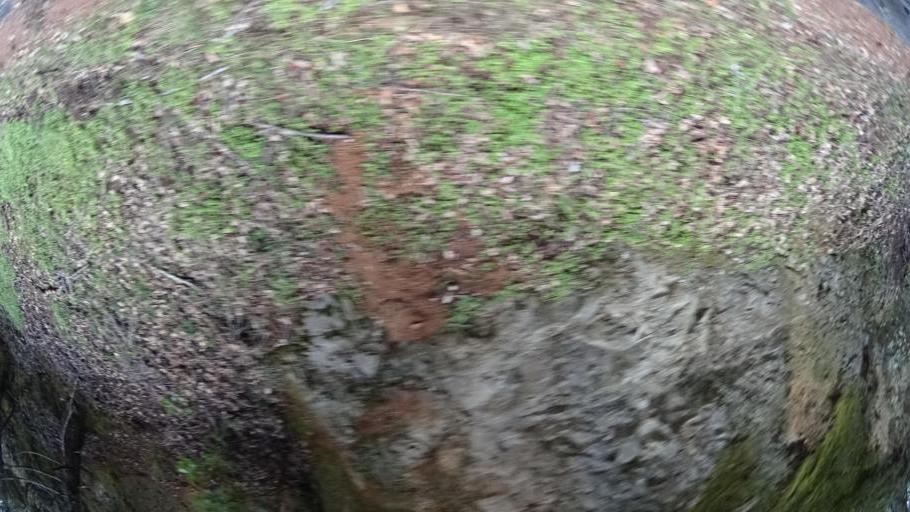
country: US
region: California
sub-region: Humboldt County
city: Blue Lake
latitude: 40.7635
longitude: -123.9274
